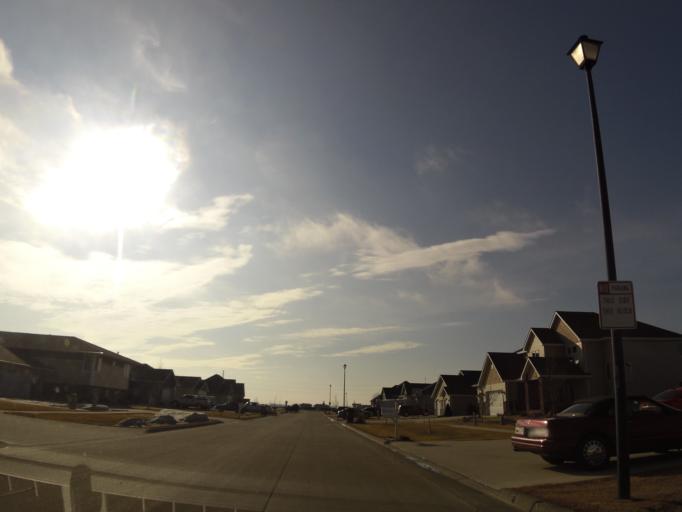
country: US
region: North Dakota
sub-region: Grand Forks County
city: Grand Forks
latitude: 47.8787
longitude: -97.0617
